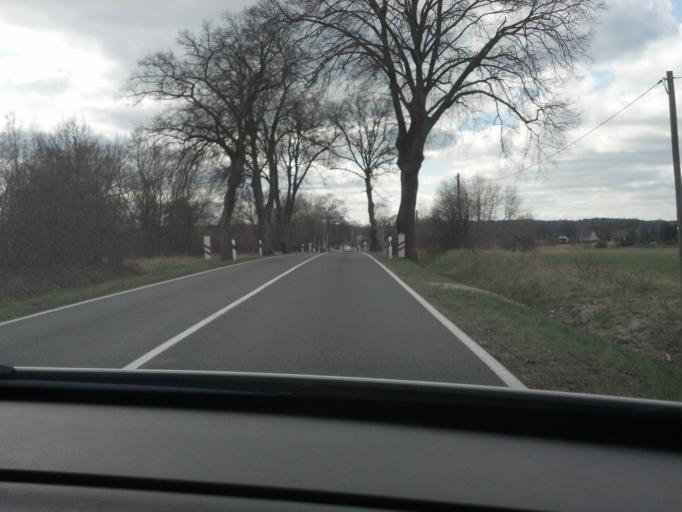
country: DE
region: Mecklenburg-Vorpommern
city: Carpin
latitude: 53.3608
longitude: 13.2564
